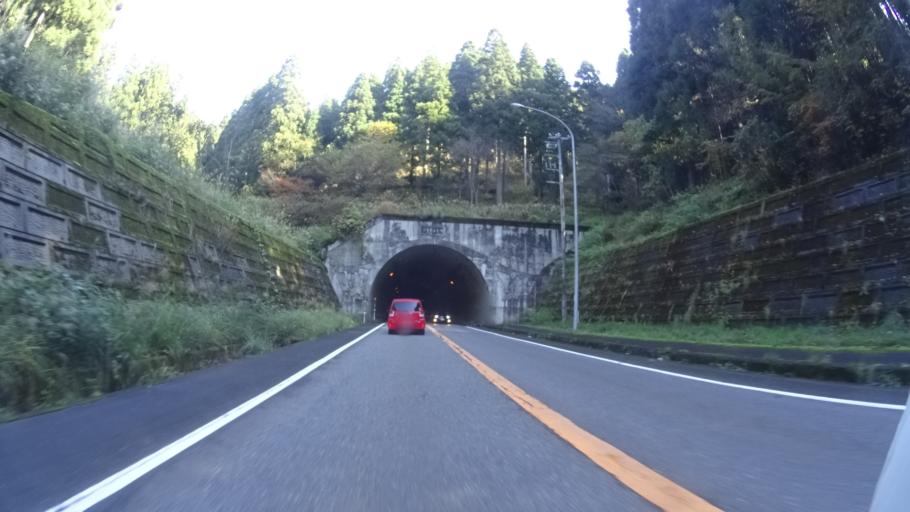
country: JP
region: Fukui
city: Ono
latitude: 35.9915
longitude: 136.4515
